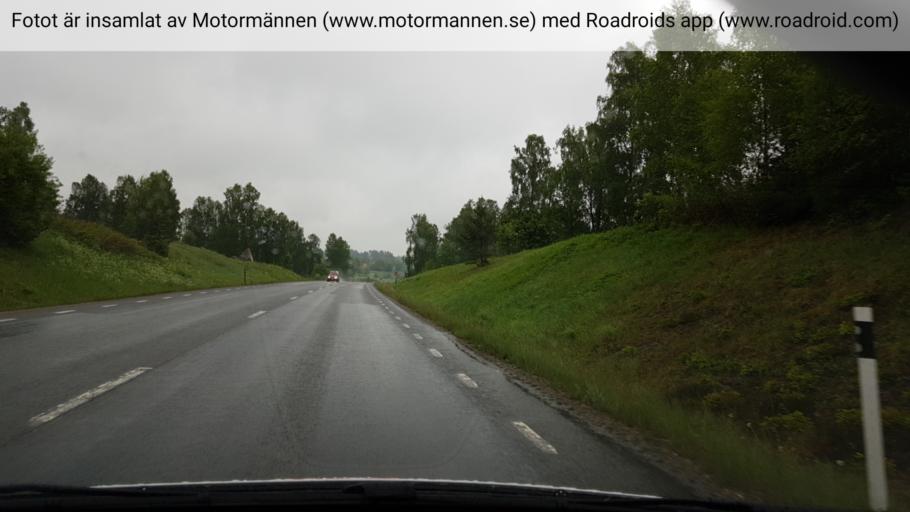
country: SE
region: Vaestra Goetaland
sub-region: Ulricehamns Kommun
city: Ulricehamn
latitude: 57.9501
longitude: 13.5162
